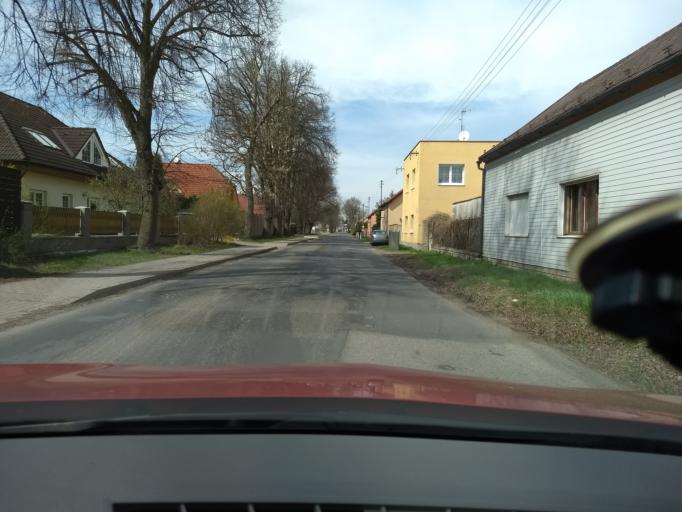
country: CZ
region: Central Bohemia
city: Jenec
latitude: 50.0465
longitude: 14.1824
